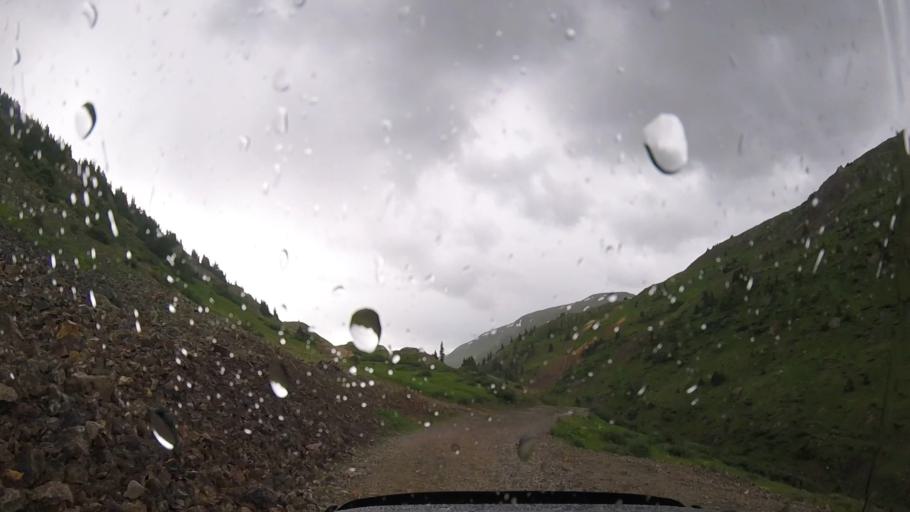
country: US
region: Colorado
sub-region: Ouray County
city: Ouray
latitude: 37.9411
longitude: -107.5735
